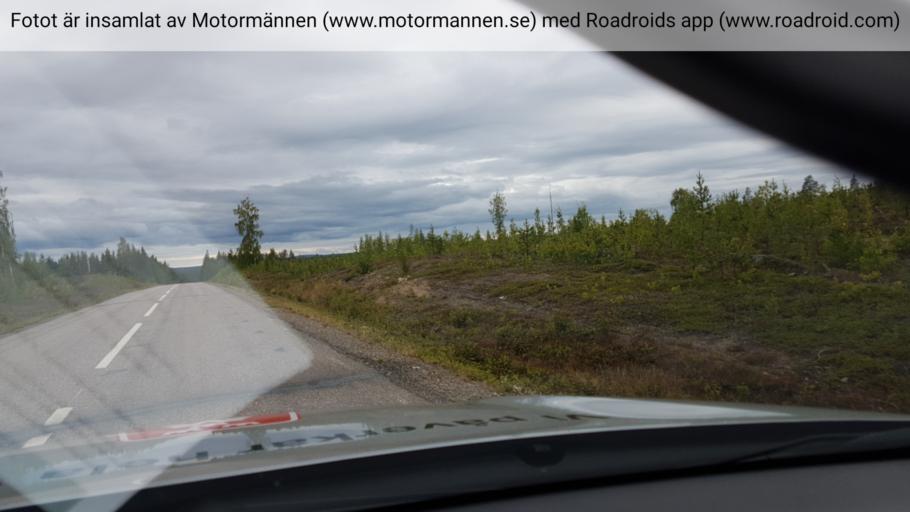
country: SE
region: Norrbotten
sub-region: Overkalix Kommun
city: OEverkalix
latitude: 66.8176
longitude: 23.0097
